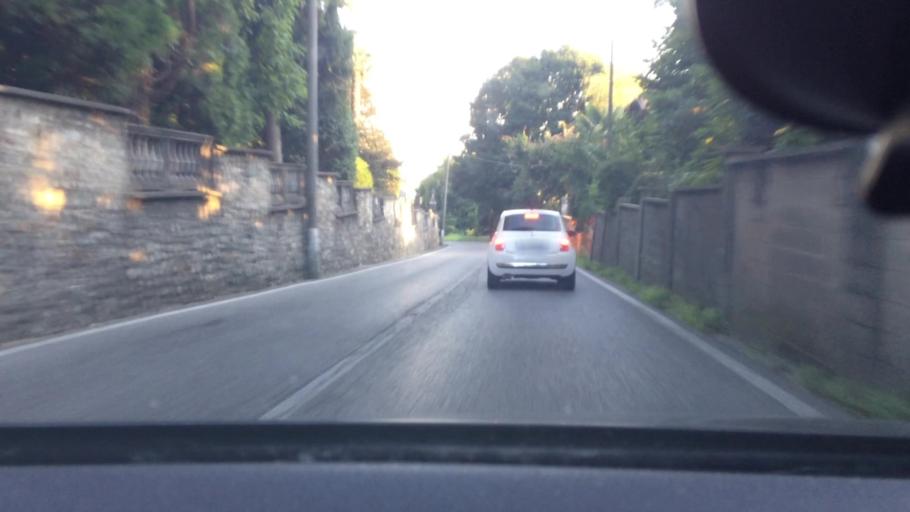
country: IT
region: Lombardy
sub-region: Provincia di Como
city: Cadorago-Caslino al Piano
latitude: 45.7344
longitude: 9.0423
